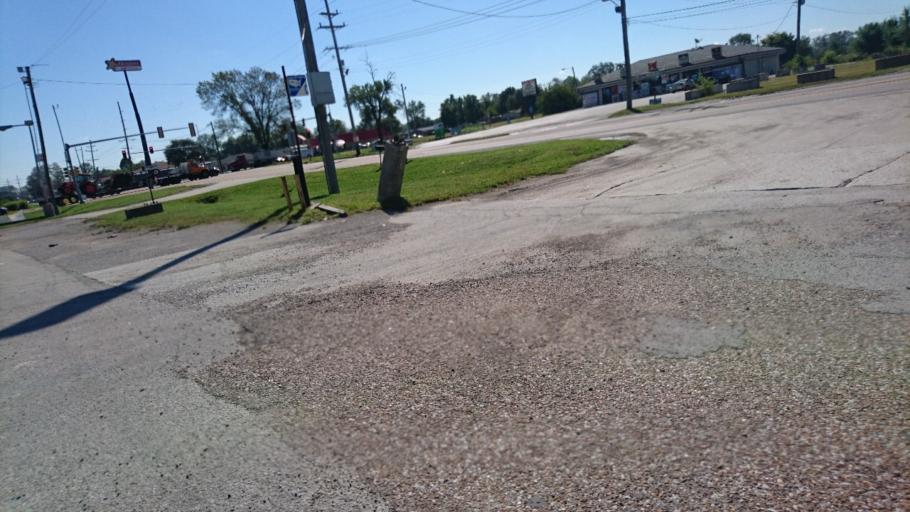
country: US
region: Illinois
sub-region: Madison County
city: Mitchell
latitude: 38.7624
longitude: -90.1255
